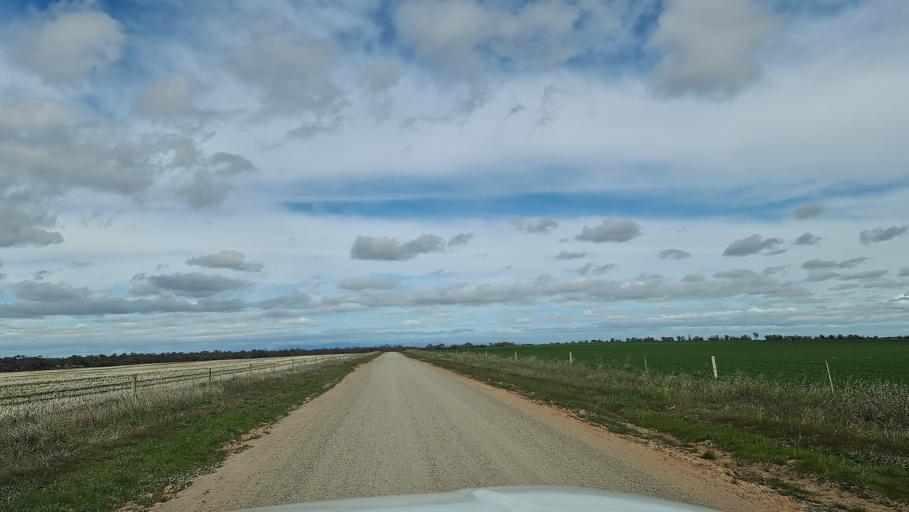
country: AU
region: Victoria
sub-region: Horsham
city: Horsham
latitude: -36.6220
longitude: 142.4118
